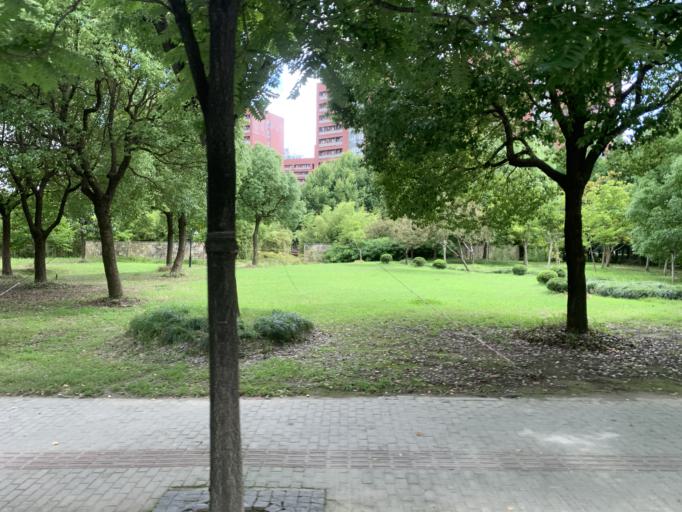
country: CN
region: Shanghai Shi
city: Huamu
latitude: 31.2047
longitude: 121.5306
